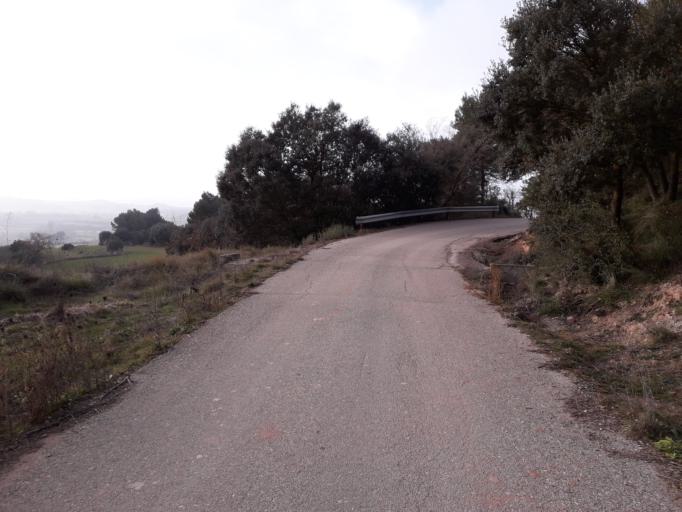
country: ES
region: Catalonia
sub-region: Provincia de Barcelona
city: Calaf
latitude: 41.6962
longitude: 1.5511
